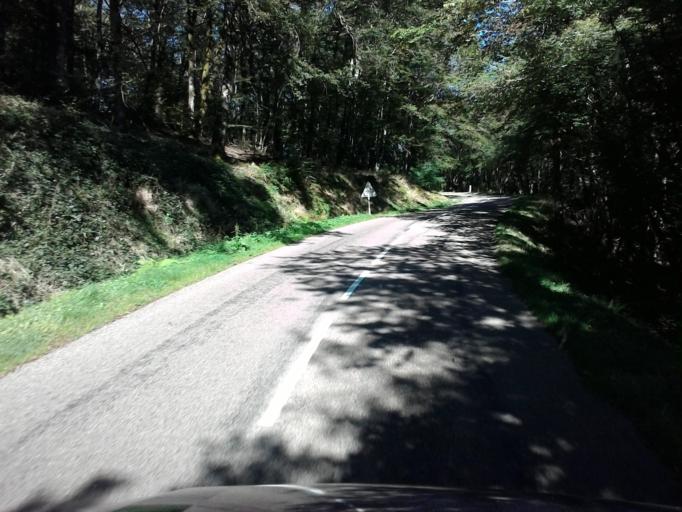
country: FR
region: Bourgogne
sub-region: Departement de la Nievre
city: Lormes
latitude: 47.2170
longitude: 3.9339
